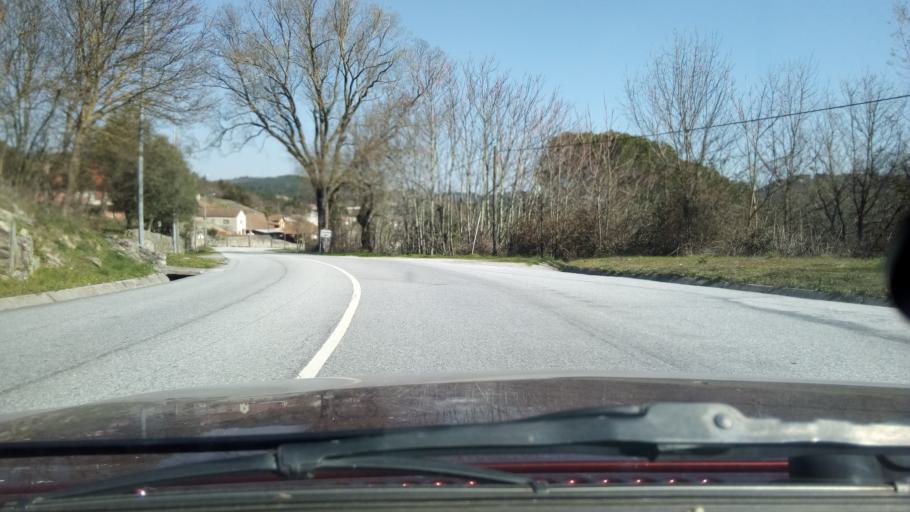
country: PT
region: Guarda
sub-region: Fornos de Algodres
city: Fornos de Algodres
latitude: 40.6108
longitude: -7.5287
